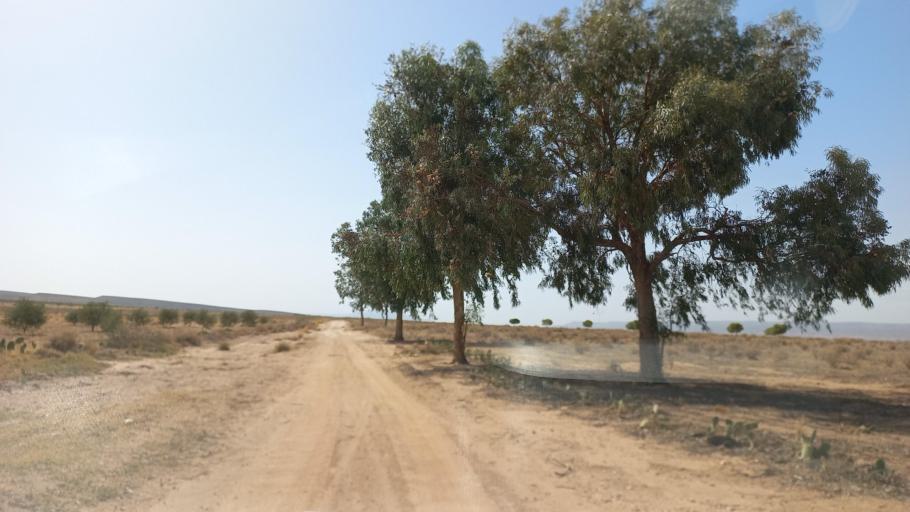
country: TN
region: Al Qasrayn
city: Kasserine
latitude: 35.2175
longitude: 9.0345
